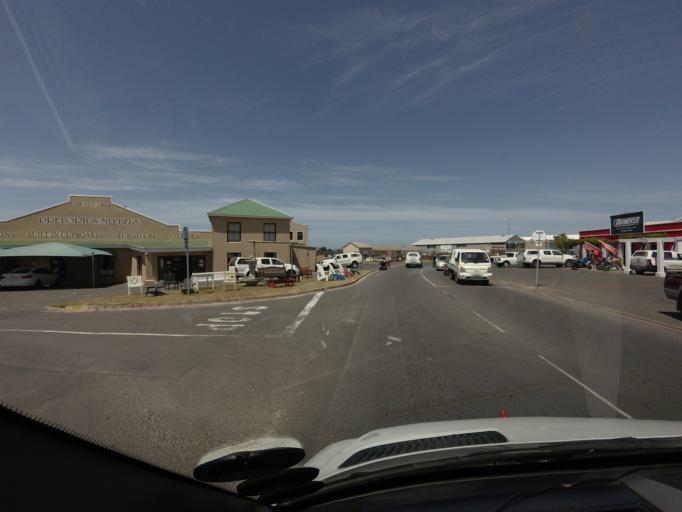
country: ZA
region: Western Cape
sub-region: Overberg District Municipality
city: Hermanus
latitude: -34.4207
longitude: 19.2248
